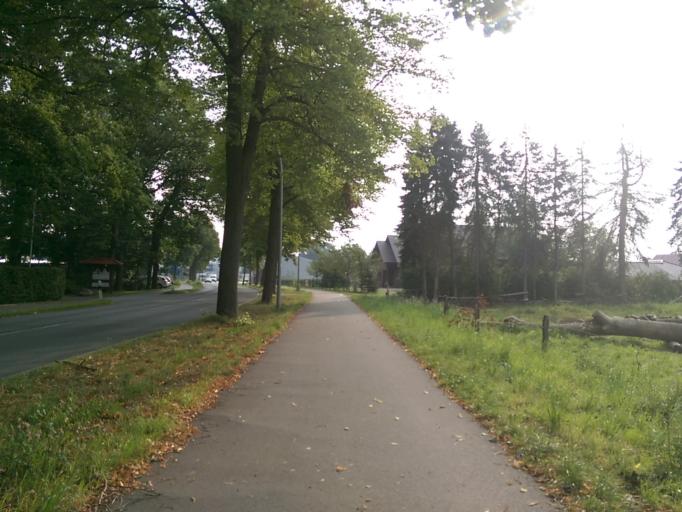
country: DE
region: North Rhine-Westphalia
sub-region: Regierungsbezirk Detmold
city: Harsewinkel
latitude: 51.9651
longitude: 8.2487
